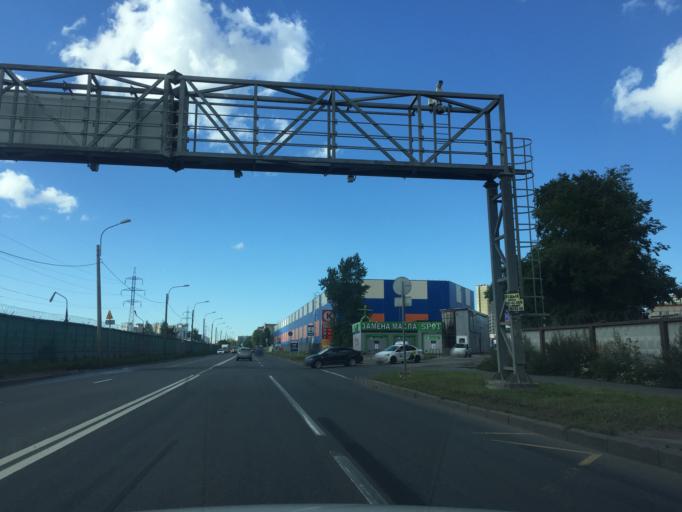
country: RU
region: St.-Petersburg
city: Dachnoye
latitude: 59.8368
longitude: 30.3049
